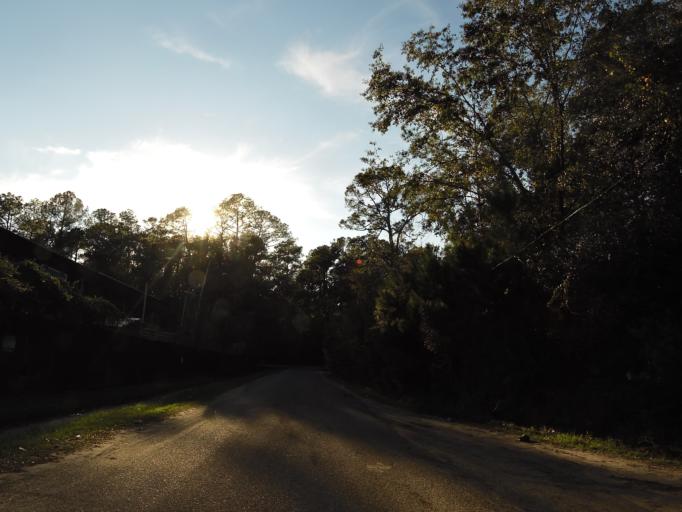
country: US
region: Florida
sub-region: Duval County
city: Jacksonville
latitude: 30.3660
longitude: -81.7318
